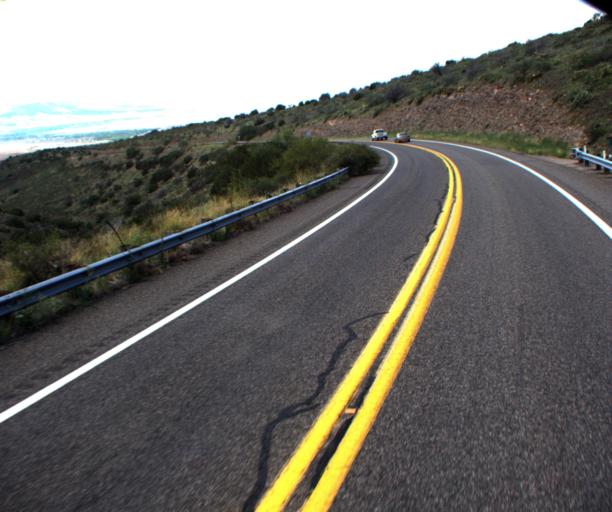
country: US
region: Arizona
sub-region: Yavapai County
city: Lake Montezuma
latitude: 34.4907
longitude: -111.7043
